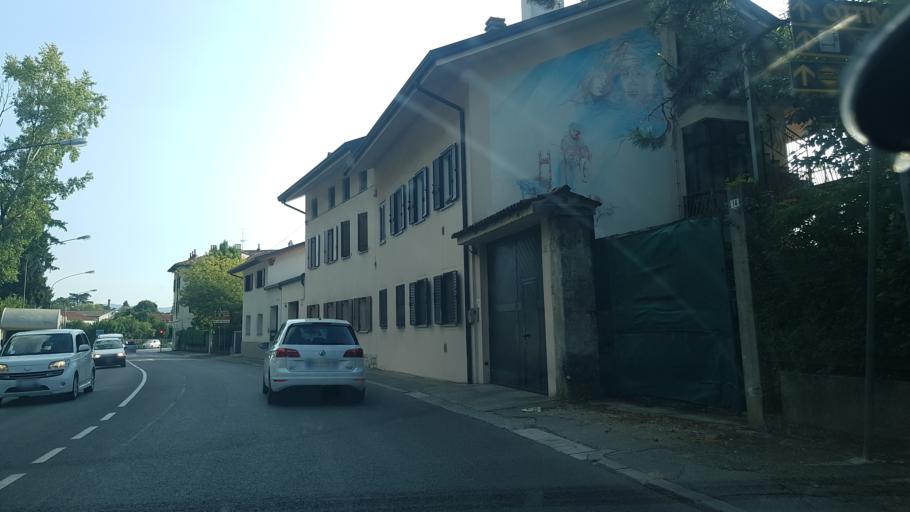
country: IT
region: Friuli Venezia Giulia
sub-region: Provincia di Gorizia
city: Gorizia
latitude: 45.9364
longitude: 13.6309
